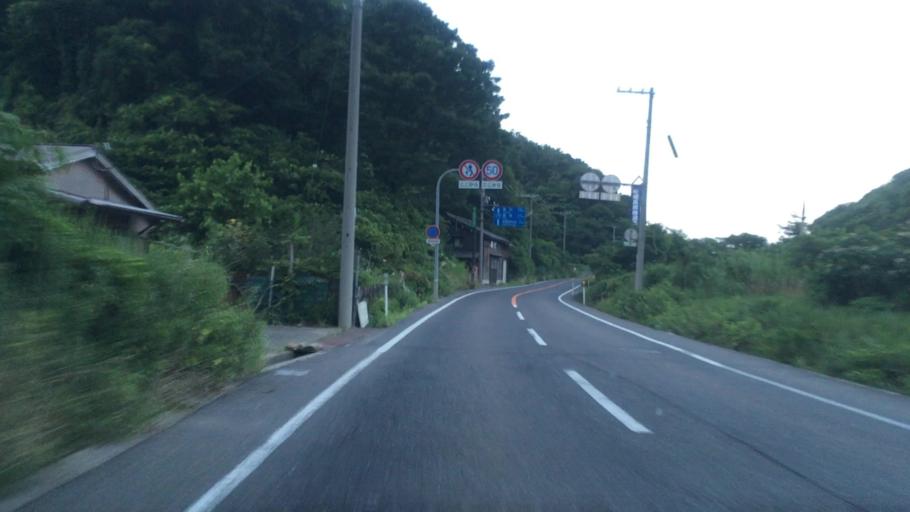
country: JP
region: Tottori
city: Tottori
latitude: 35.6156
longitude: 134.3939
